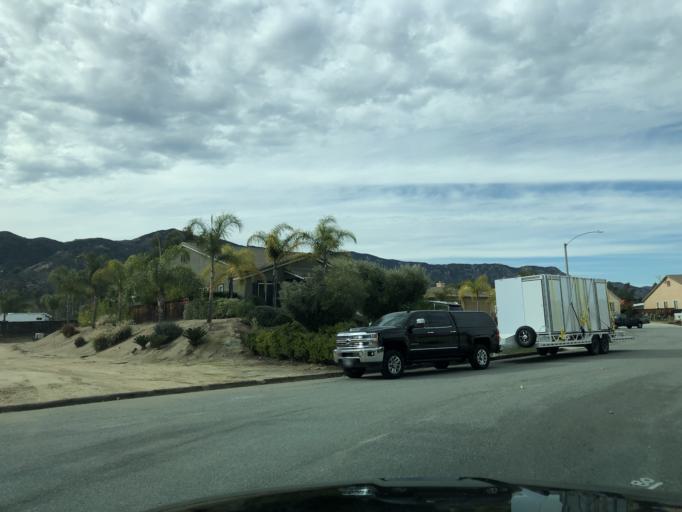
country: US
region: California
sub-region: Riverside County
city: Wildomar
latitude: 33.6083
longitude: -117.2891
